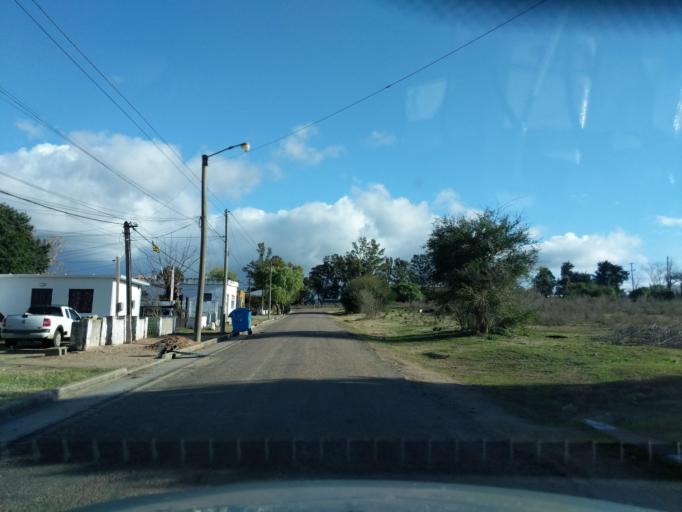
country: UY
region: Florida
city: Florida
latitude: -34.1077
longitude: -56.2216
